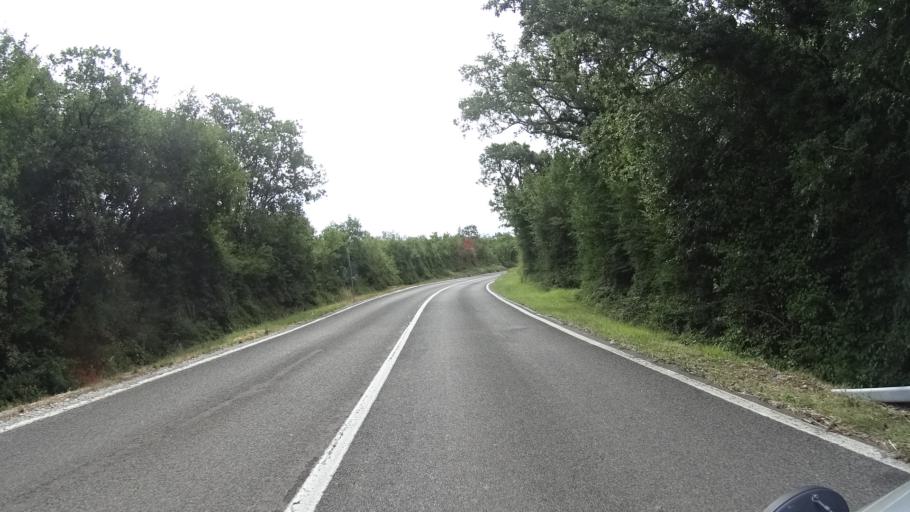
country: HR
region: Istarska
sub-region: Grad Rovinj
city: Rovinj
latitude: 45.1175
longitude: 13.7652
